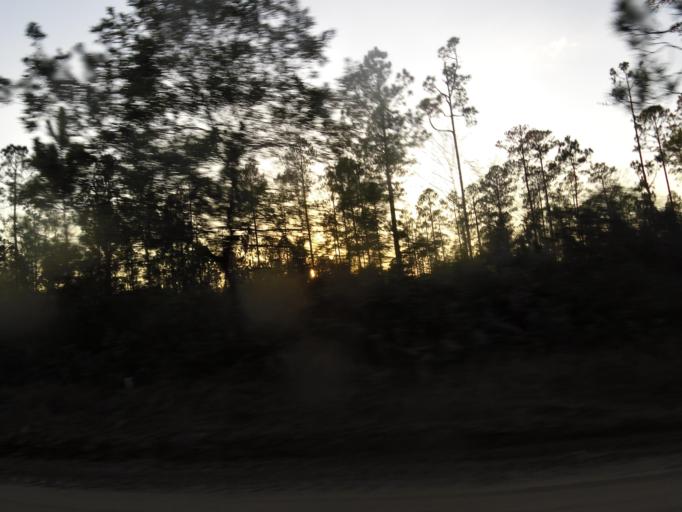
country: US
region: Florida
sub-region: Clay County
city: Green Cove Springs
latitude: 29.8455
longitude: -81.7971
